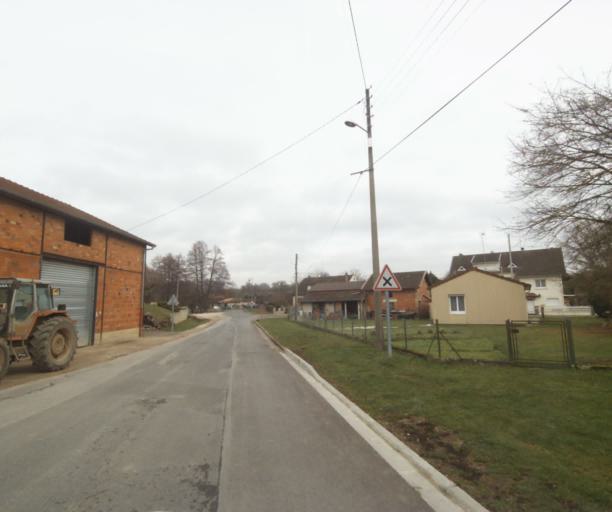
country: FR
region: Champagne-Ardenne
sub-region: Departement de la Marne
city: Sermaize-les-Bains
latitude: 48.7384
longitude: 4.9051
